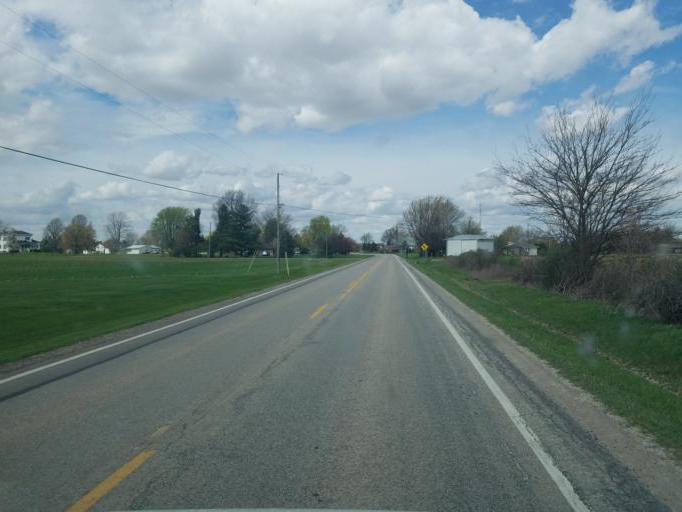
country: US
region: Ohio
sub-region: Crawford County
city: Bucyrus
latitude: 40.8594
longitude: -82.9971
